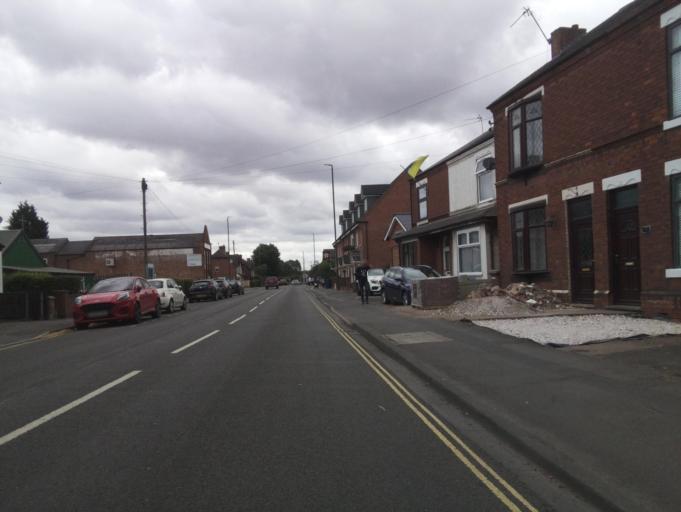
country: GB
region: England
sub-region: Derbyshire
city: Long Eaton
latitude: 52.8875
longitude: -1.2878
